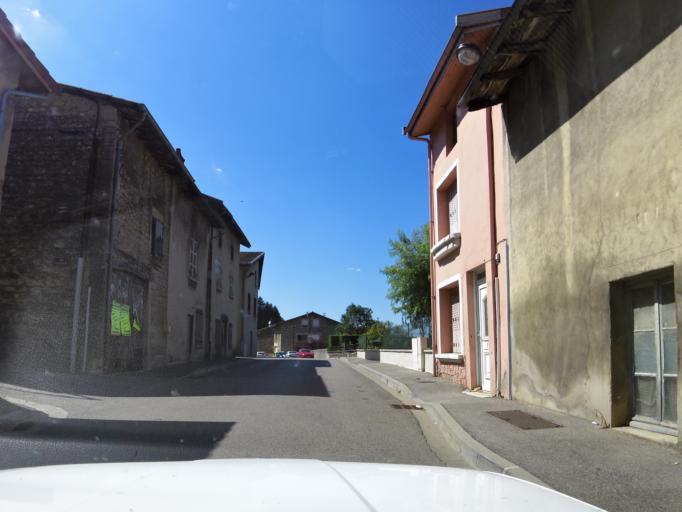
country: FR
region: Rhone-Alpes
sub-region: Departement de l'Ain
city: Amberieu-en-Bugey
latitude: 45.9452
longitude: 5.3530
